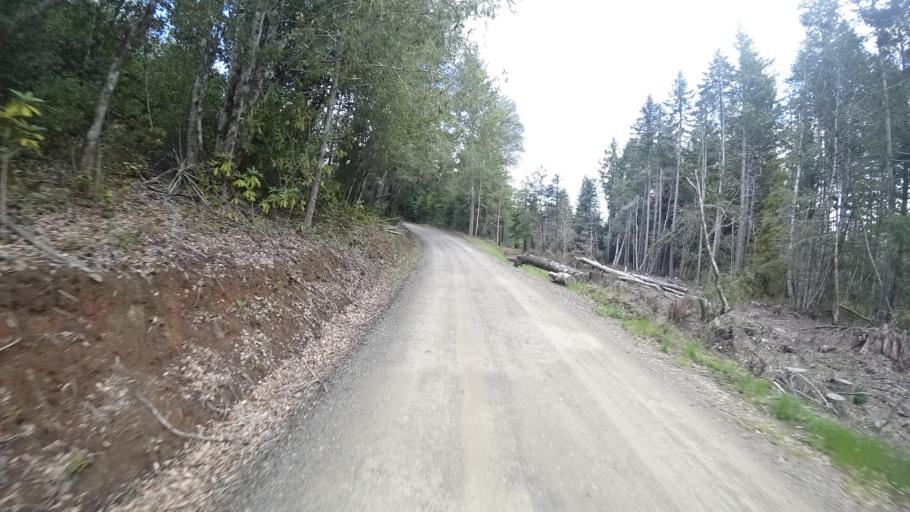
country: US
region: California
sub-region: Humboldt County
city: Blue Lake
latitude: 40.7694
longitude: -123.9554
